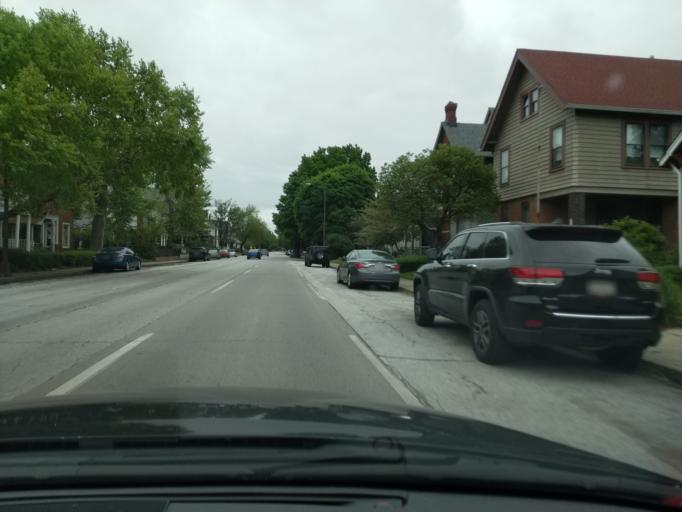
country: US
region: Indiana
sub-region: Marion County
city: Indianapolis
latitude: 39.7903
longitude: -86.1537
